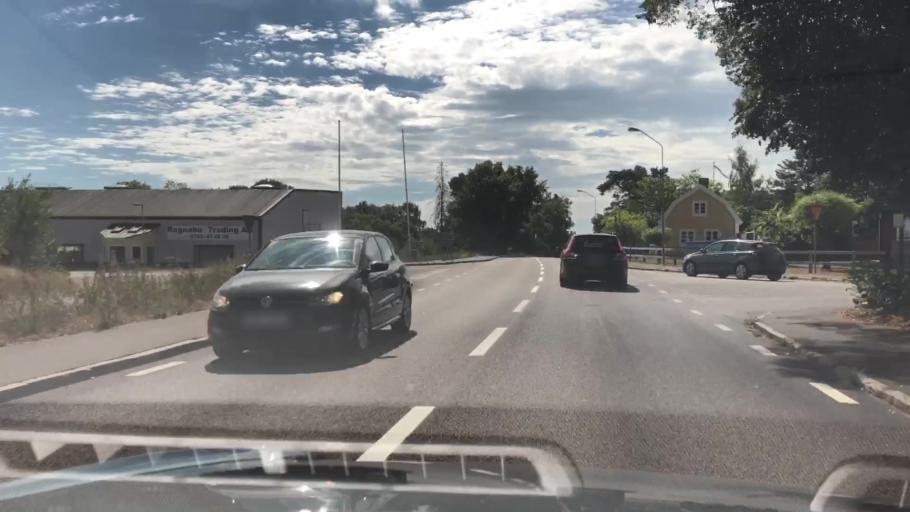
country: SE
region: Kalmar
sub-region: Torsas Kommun
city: Torsas
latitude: 56.3909
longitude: 16.0667
